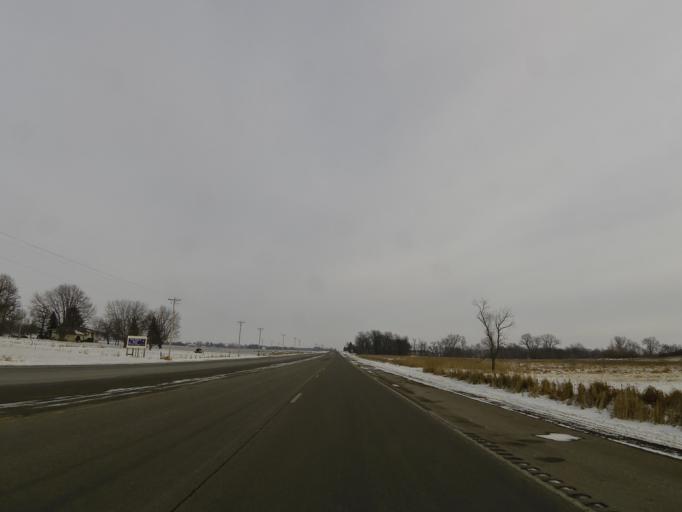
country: US
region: Minnesota
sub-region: McLeod County
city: Lester Prairie
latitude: 44.9068
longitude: -94.1256
